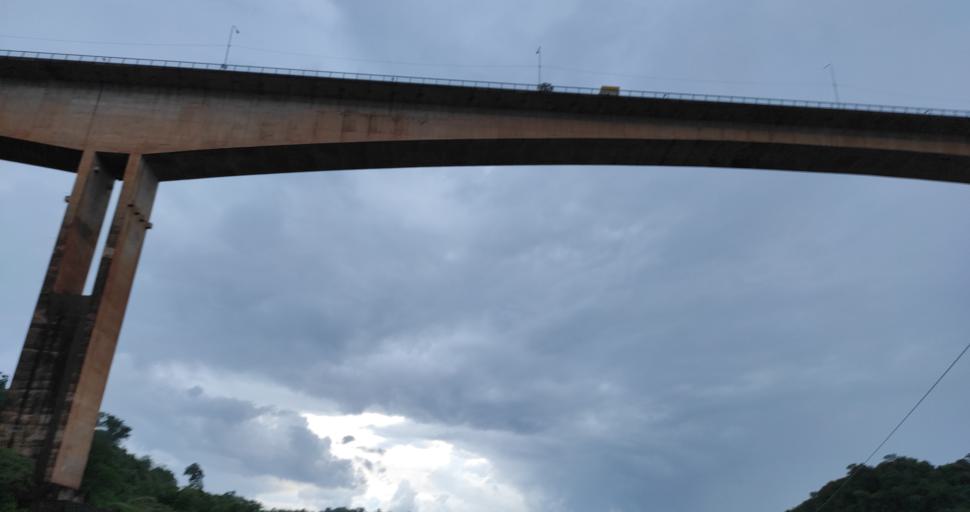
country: AR
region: Misiones
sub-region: Departamento de Iguazu
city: Puerto Iguazu
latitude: -25.5888
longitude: -54.5604
